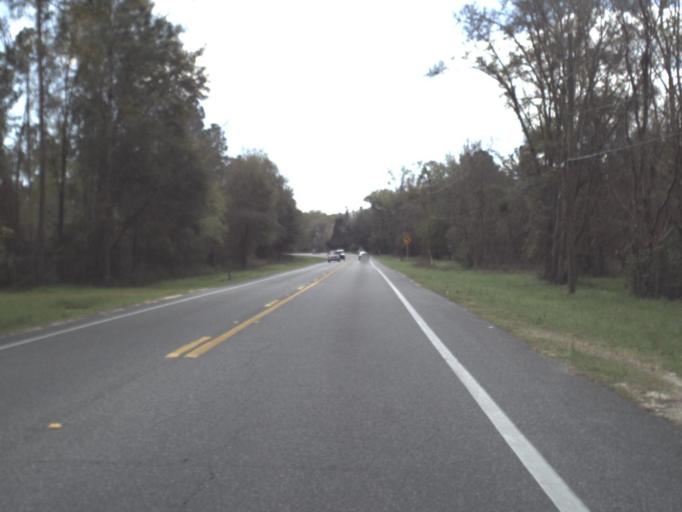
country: US
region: Florida
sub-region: Wakulla County
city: Crawfordville
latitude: 30.1316
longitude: -84.3879
